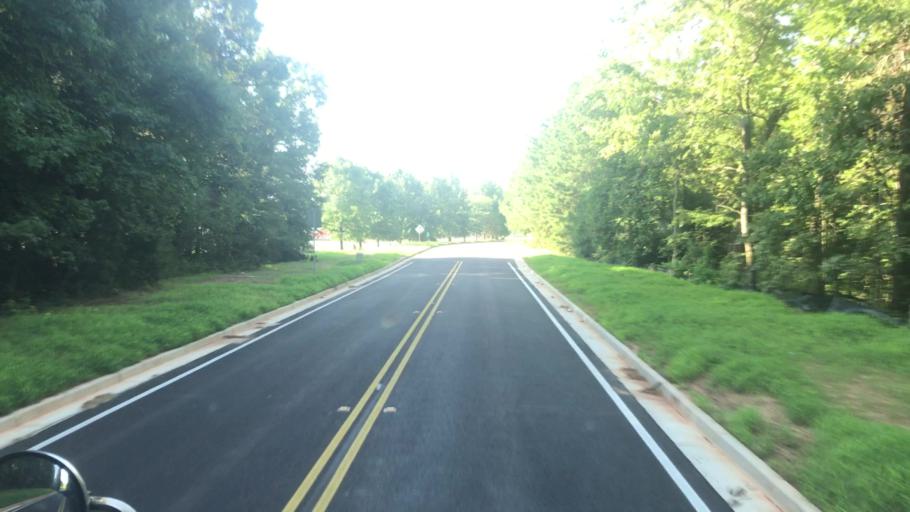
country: US
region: Georgia
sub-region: Henry County
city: McDonough
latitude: 33.3944
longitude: -84.1685
